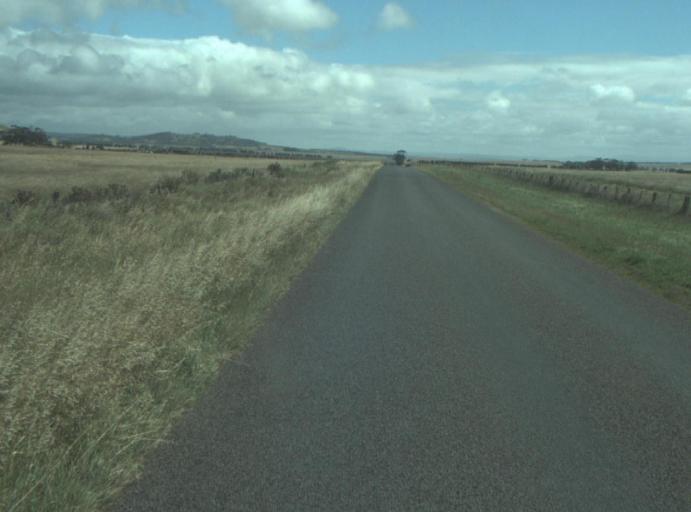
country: AU
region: Victoria
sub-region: Greater Geelong
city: Lara
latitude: -37.9404
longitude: 144.3098
